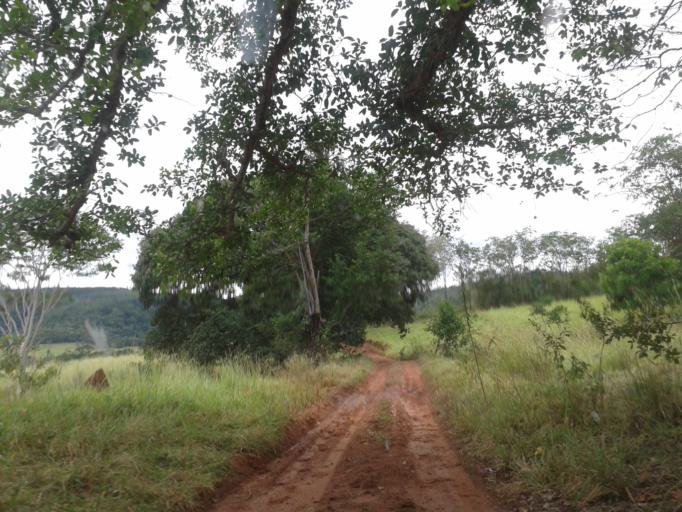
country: BR
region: Minas Gerais
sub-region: Campina Verde
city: Campina Verde
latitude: -19.4666
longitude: -49.5893
